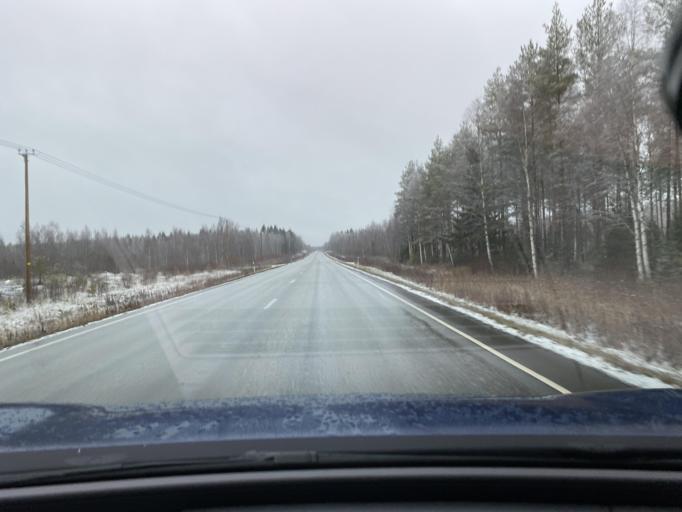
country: FI
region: Northern Ostrobothnia
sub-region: Oulu
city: Kiiminki
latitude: 65.1349
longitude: 25.8201
